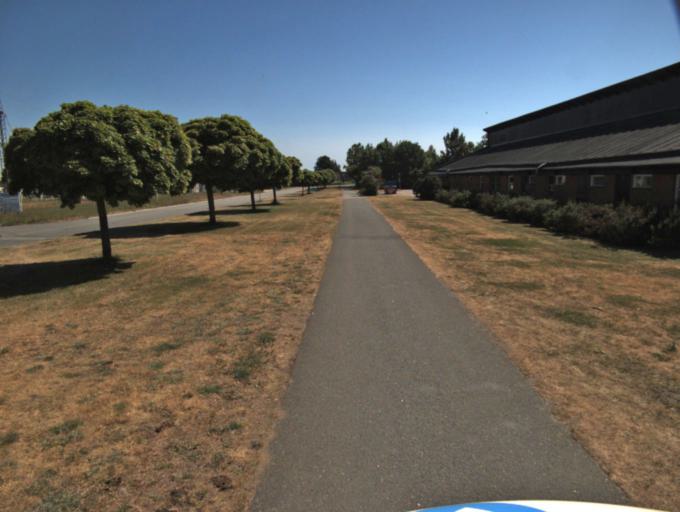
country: SE
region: Skane
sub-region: Kristianstads Kommun
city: Ahus
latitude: 55.9296
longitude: 14.2855
